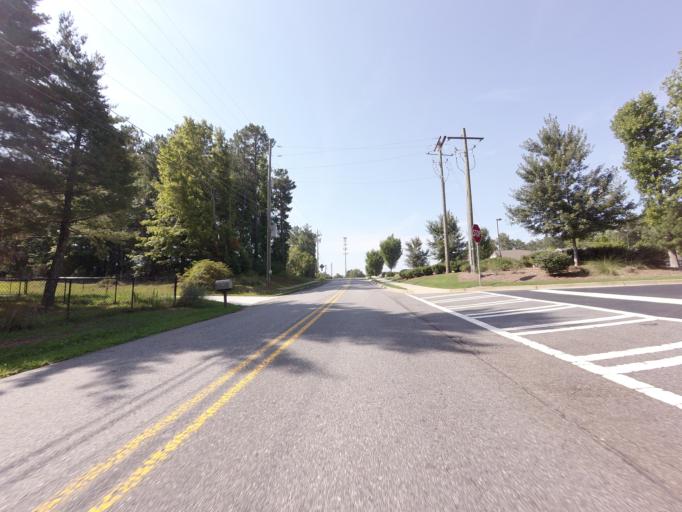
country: US
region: Georgia
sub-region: Fulton County
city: Johns Creek
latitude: 34.0667
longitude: -84.2149
